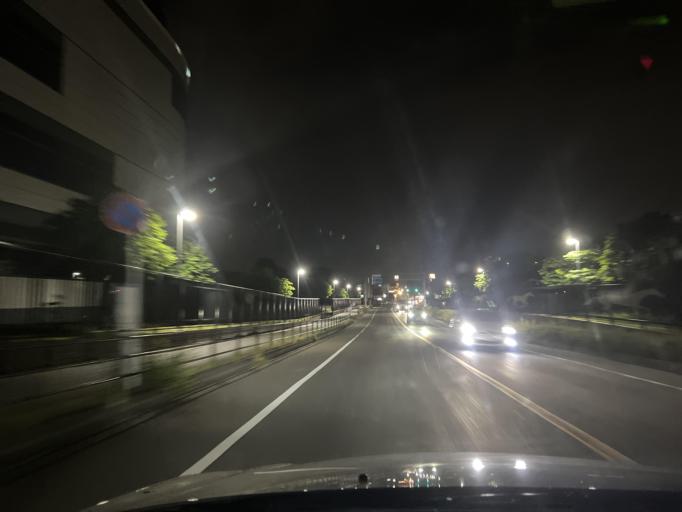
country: JP
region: Chiba
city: Funabashi
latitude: 35.7243
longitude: 139.9591
